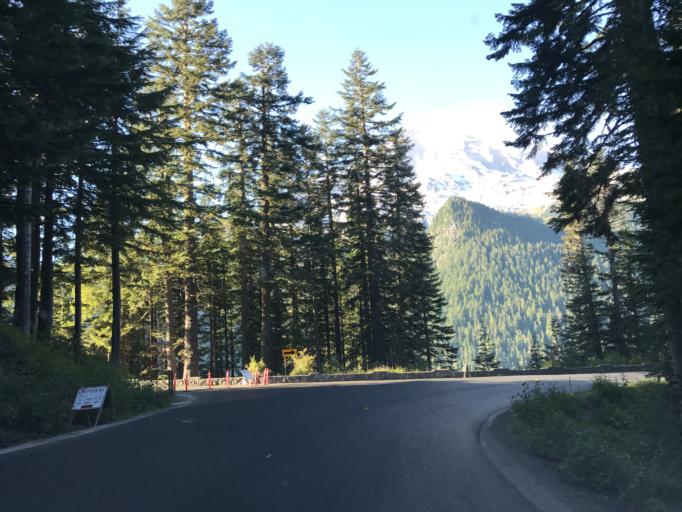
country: US
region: Washington
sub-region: Pierce County
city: Buckley
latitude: 46.7716
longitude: -121.7765
